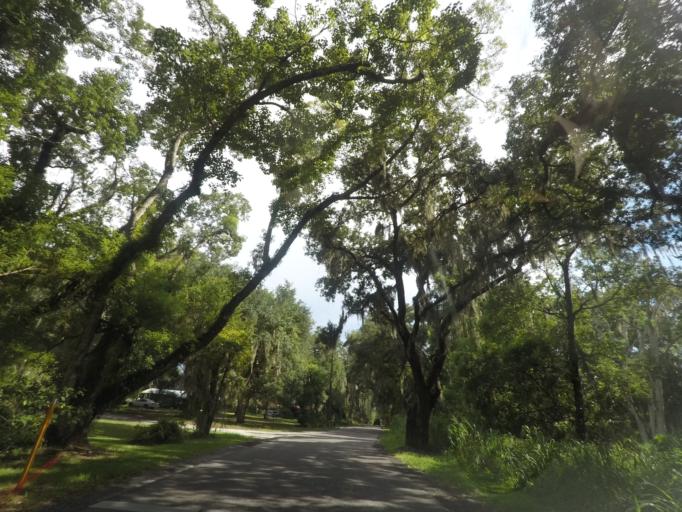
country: US
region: Florida
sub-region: Osceola County
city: Kissimmee
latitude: 28.3211
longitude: -81.4626
